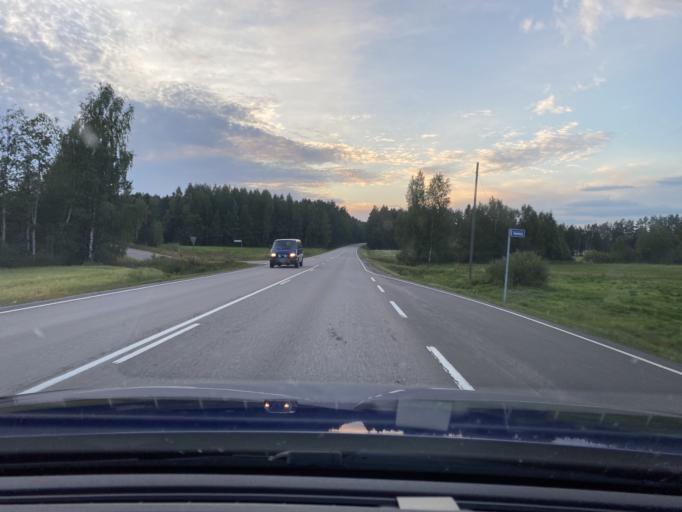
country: FI
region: Satakunta
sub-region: Pohjois-Satakunta
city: Honkajoki
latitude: 61.9050
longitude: 22.2719
